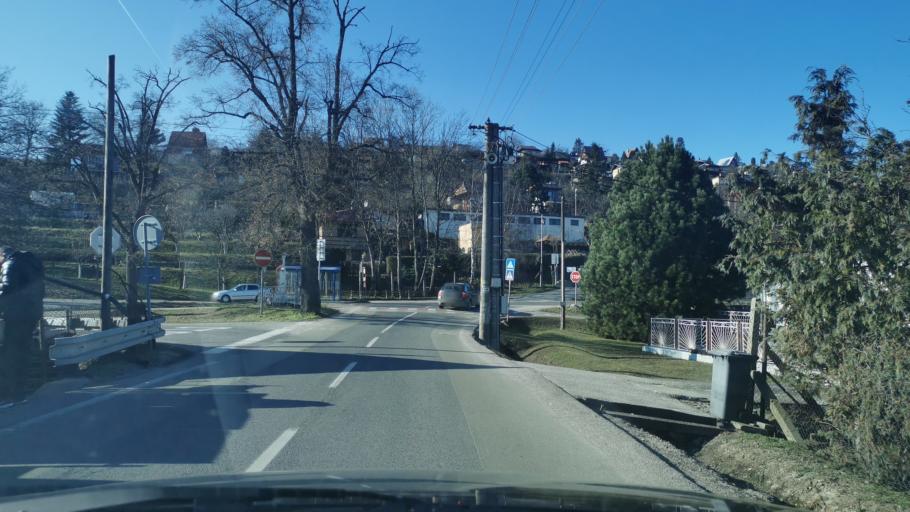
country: SK
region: Trnavsky
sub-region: Okres Senica
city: Senica
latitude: 48.6938
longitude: 17.3986
